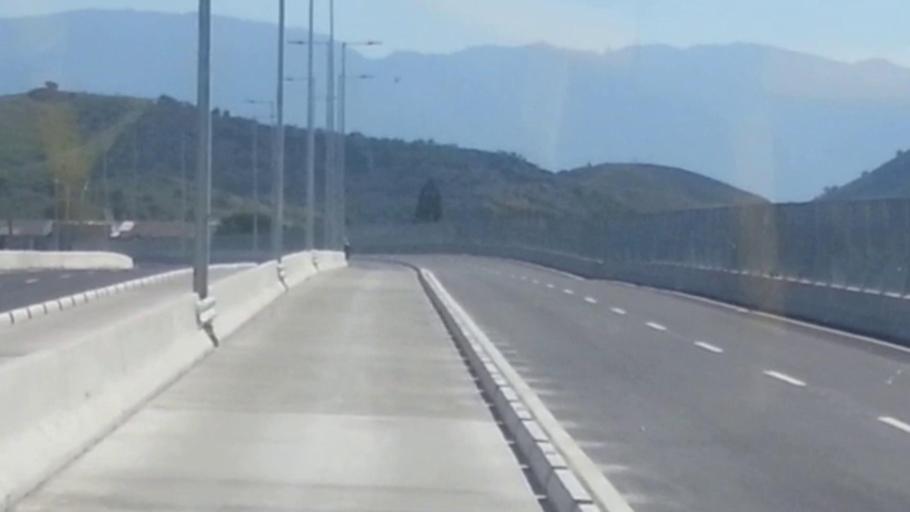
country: BR
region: Rio de Janeiro
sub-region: Nilopolis
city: Nilopolis
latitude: -22.8746
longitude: -43.4065
